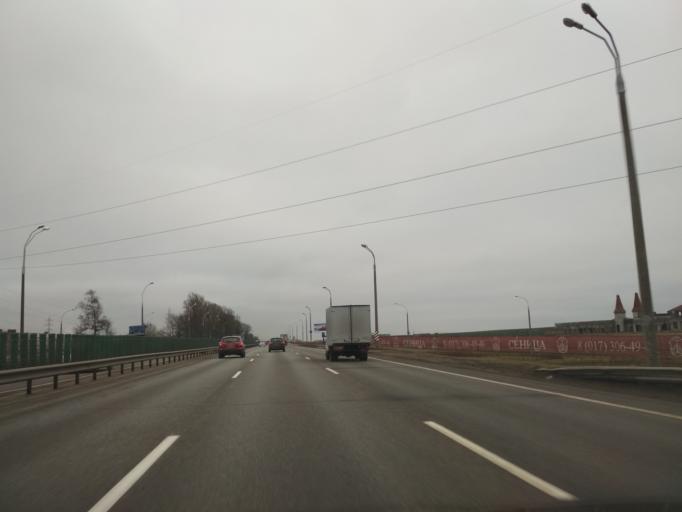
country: BY
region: Minsk
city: Yubilyeyny
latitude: 53.8387
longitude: 27.5028
